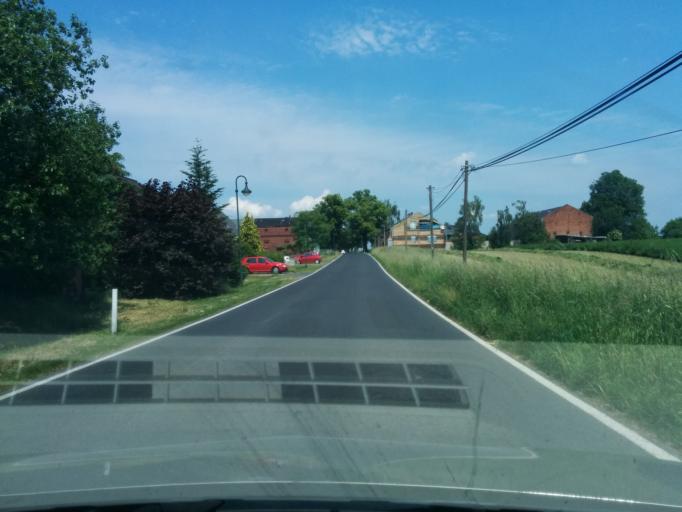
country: DE
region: Brandenburg
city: Bernau bei Berlin
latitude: 52.6309
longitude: 13.5745
